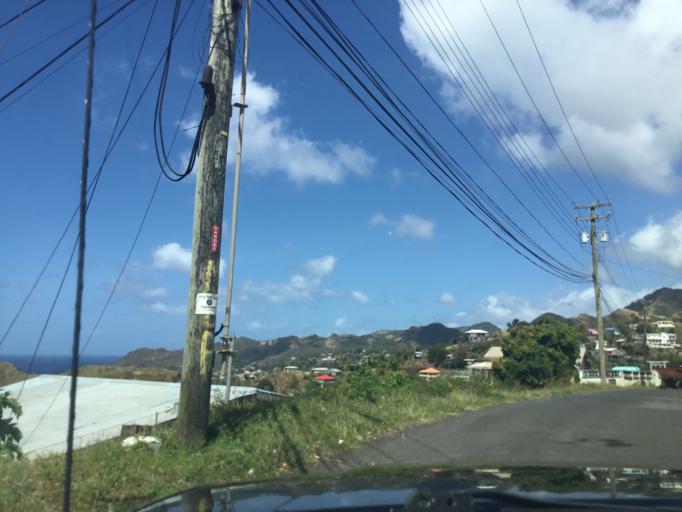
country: VC
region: Saint George
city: Kingstown Park
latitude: 13.1607
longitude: -61.2386
